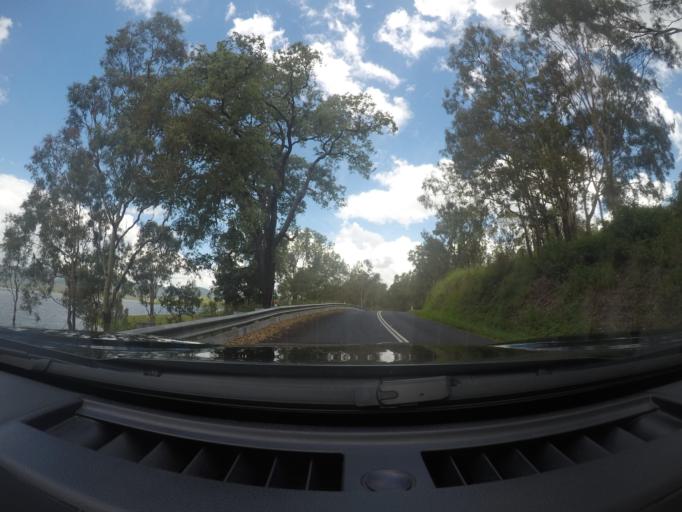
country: AU
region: Queensland
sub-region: Moreton Bay
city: Woodford
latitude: -27.0752
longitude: 152.5658
